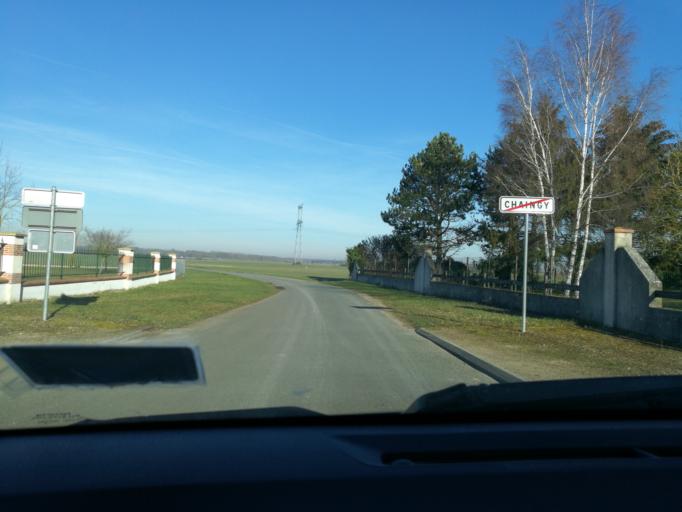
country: FR
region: Centre
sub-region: Departement du Loiret
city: Chaingy
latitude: 47.8829
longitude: 1.7629
